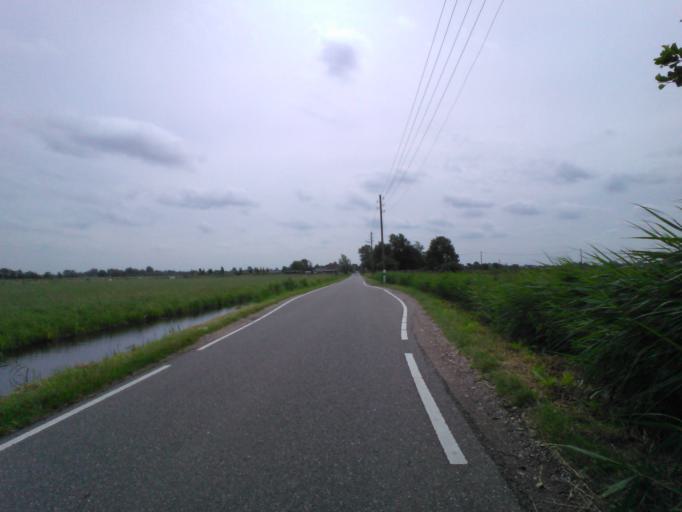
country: NL
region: South Holland
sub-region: Molenwaard
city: Nieuw-Lekkerland
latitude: 51.9520
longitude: 4.6969
